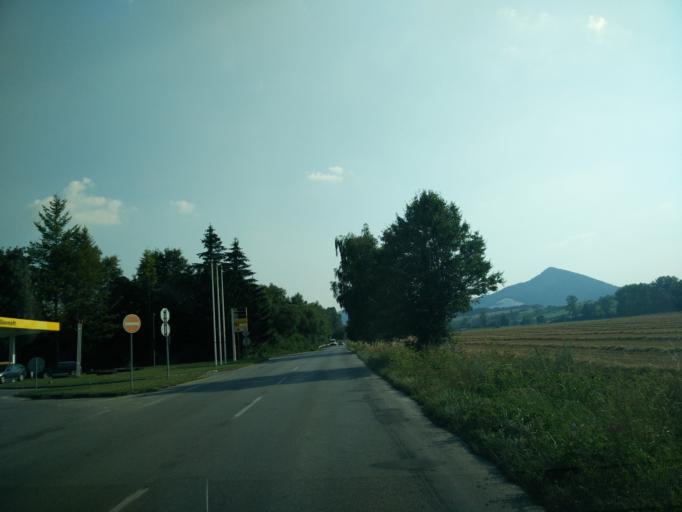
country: SK
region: Zilinsky
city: Rajec
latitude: 49.0778
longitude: 18.6313
